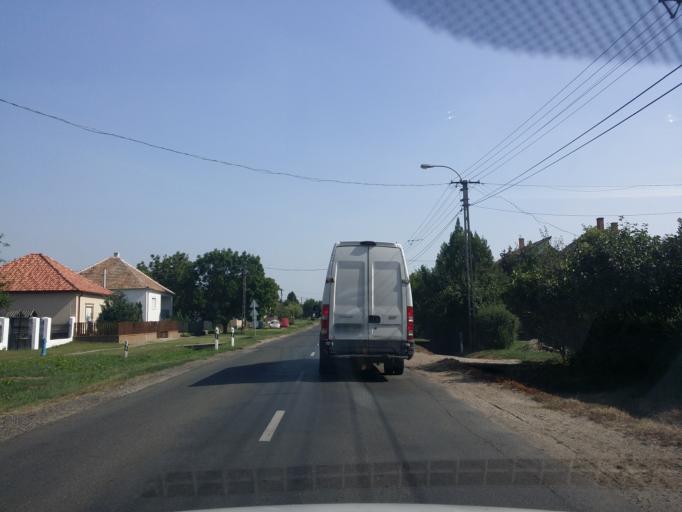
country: HU
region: Fejer
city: Mezofalva
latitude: 46.9290
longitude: 18.7857
